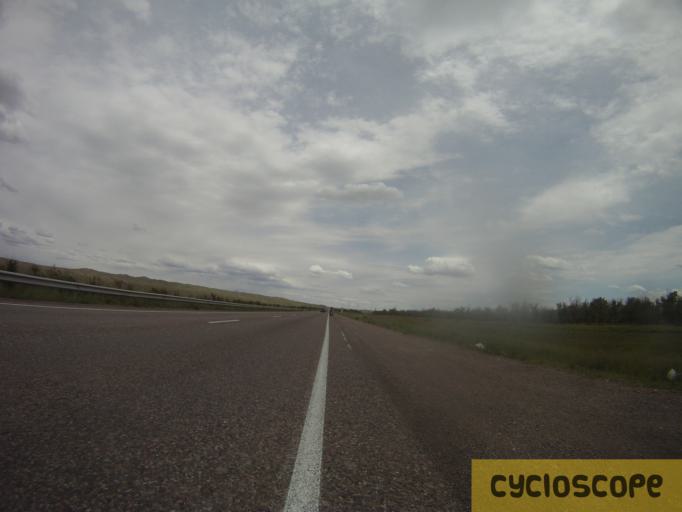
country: KZ
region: Zhambyl
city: Georgiyevka
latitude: 43.3227
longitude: 74.9351
